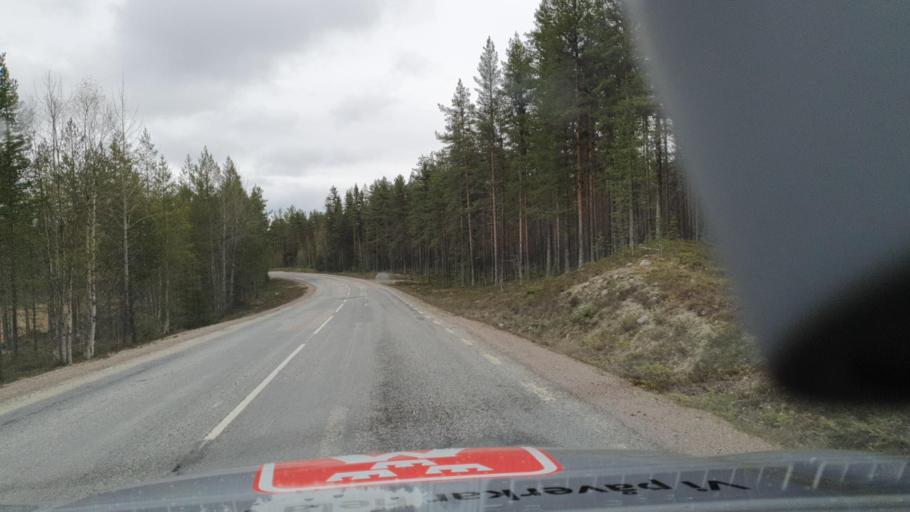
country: SE
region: Vaesternorrland
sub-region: Solleftea Kommun
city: Solleftea
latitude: 63.6619
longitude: 17.2634
